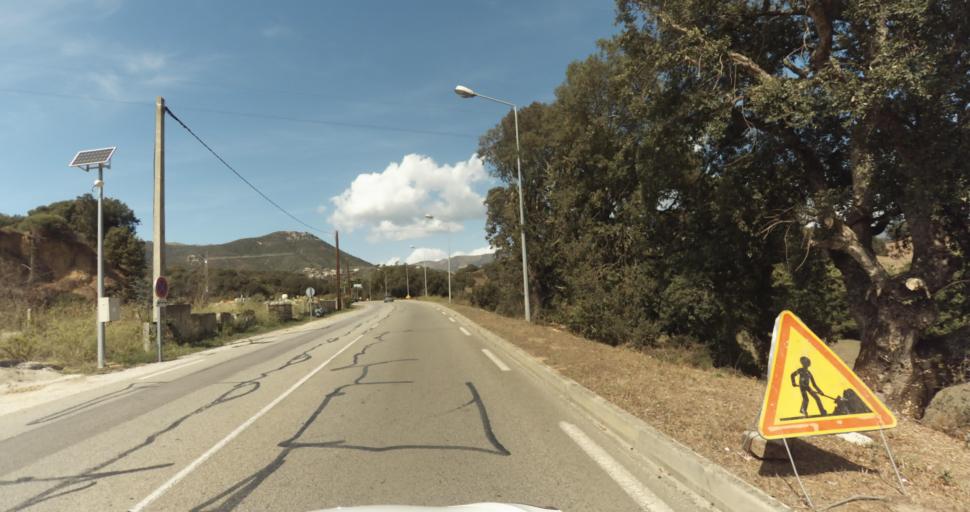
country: FR
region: Corsica
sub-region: Departement de la Corse-du-Sud
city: Afa
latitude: 41.9566
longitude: 8.7821
